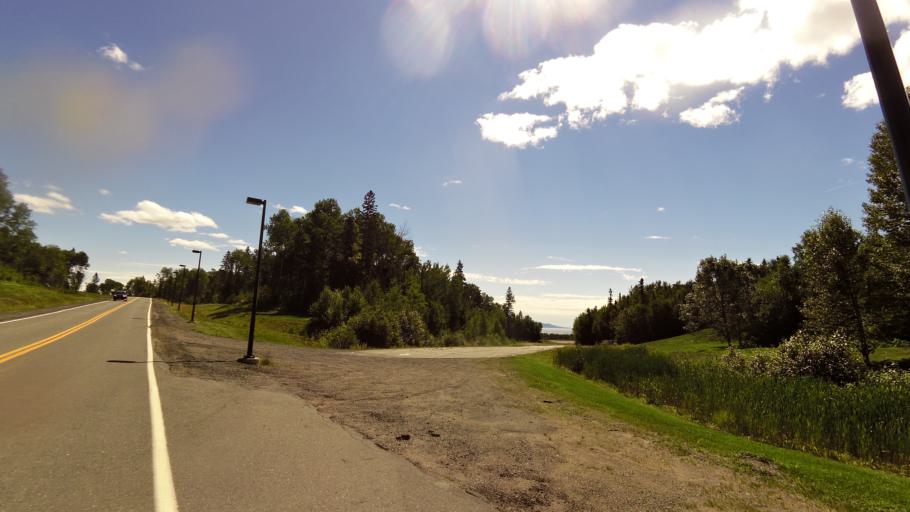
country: CA
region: Ontario
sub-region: Thunder Bay District
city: Thunder Bay
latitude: 48.4863
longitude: -89.1689
